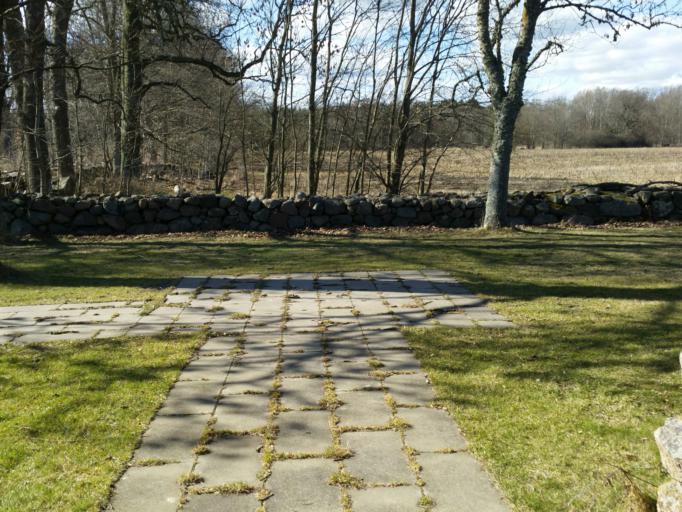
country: SE
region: Kalmar
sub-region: Monsteras Kommun
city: Moensteras
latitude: 57.0187
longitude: 16.4379
